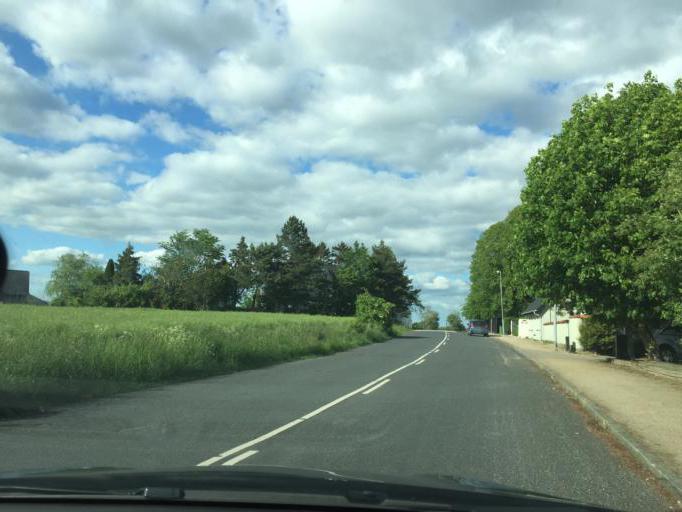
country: DK
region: South Denmark
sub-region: Odense Kommune
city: Bellinge
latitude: 55.3344
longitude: 10.3085
